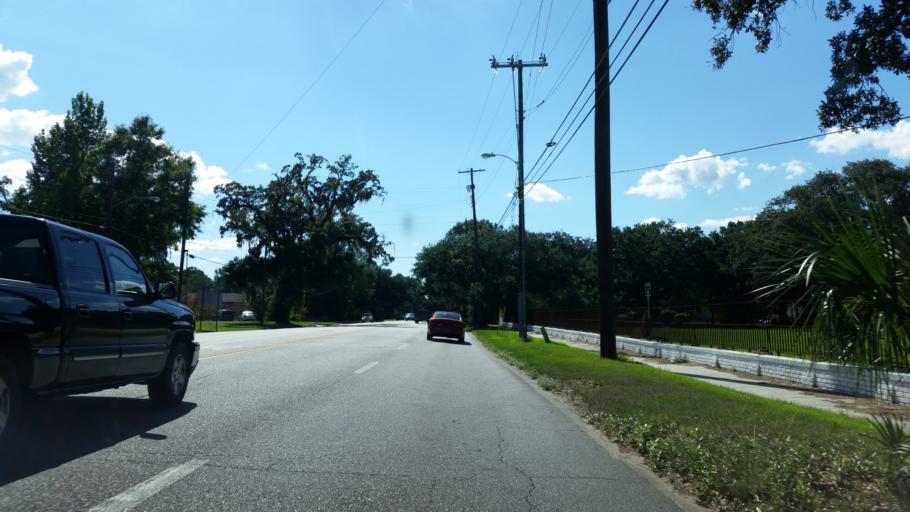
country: US
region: Alabama
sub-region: Mobile County
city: Mobile
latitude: 30.6925
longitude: -88.0731
